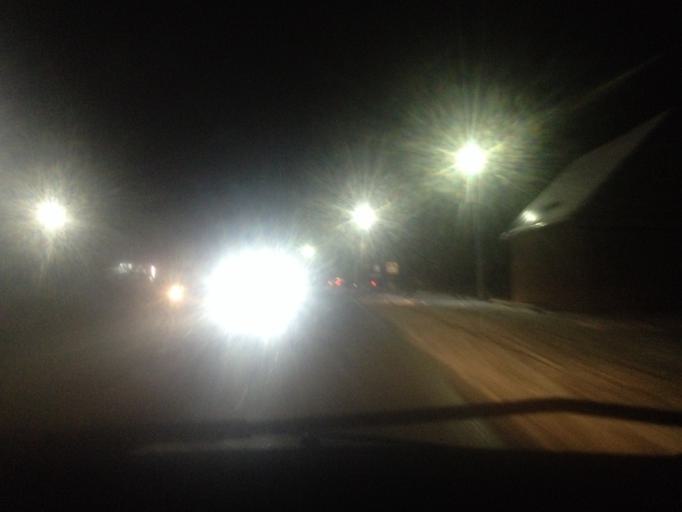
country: RU
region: Tula
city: Barsuki
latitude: 54.2633
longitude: 37.4843
